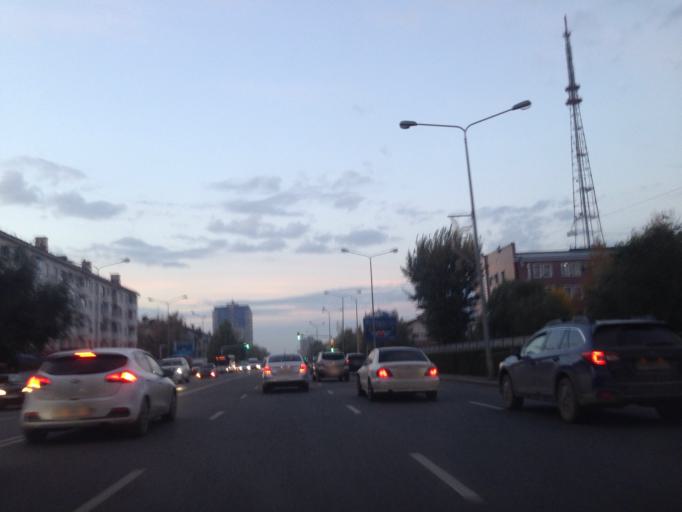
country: KZ
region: Astana Qalasy
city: Astana
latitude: 51.1803
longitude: 71.4099
